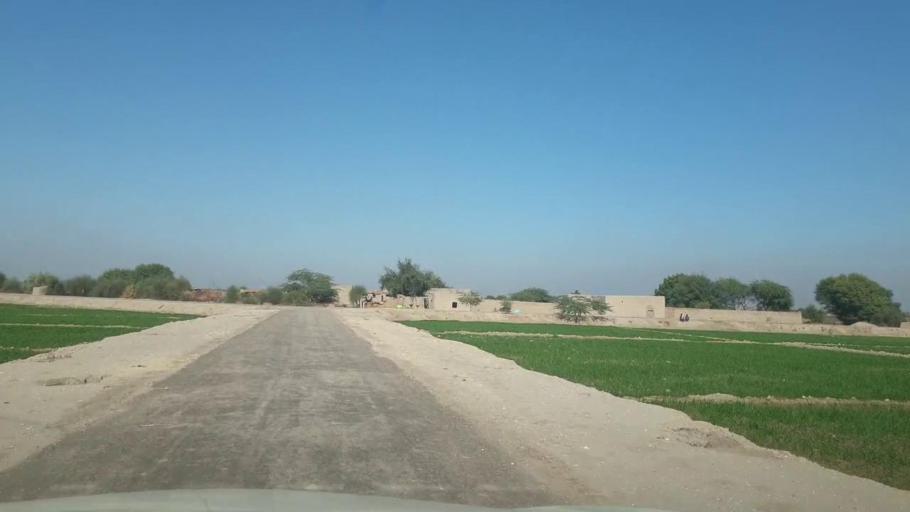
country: PK
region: Sindh
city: Bhan
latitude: 26.5657
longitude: 67.6913
